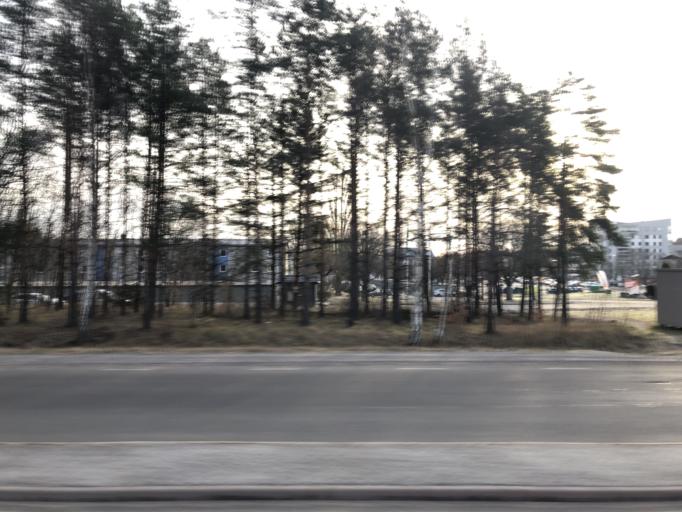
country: SE
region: Stockholm
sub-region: Jarfalla Kommun
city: Jakobsberg
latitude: 59.4142
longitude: 17.7977
